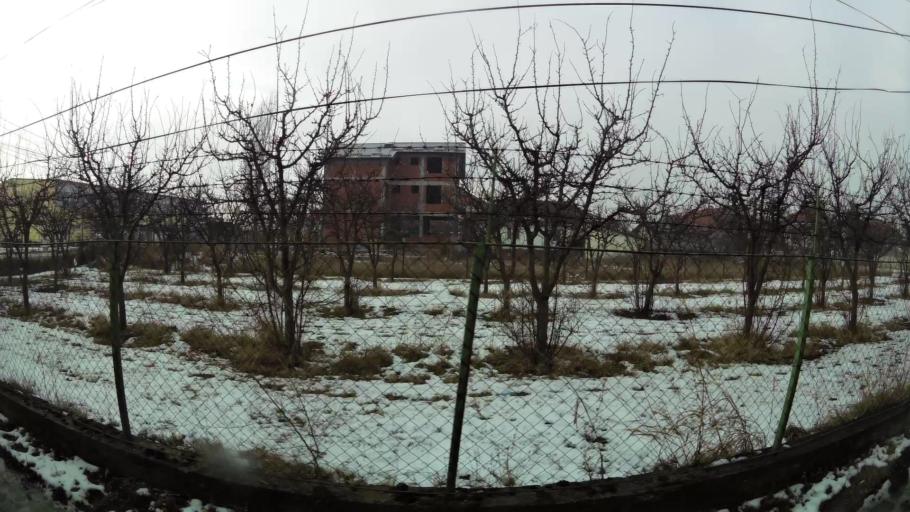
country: MK
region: Ilinden
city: Ilinden
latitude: 41.9915
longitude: 21.5833
